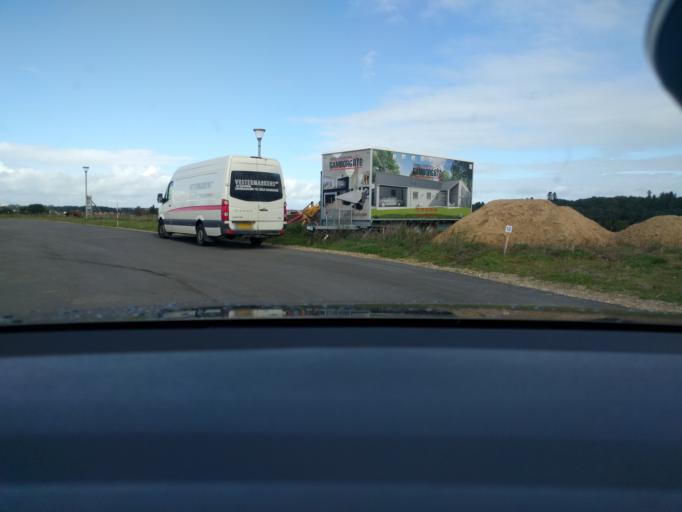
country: DK
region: Central Jutland
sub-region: Viborg Kommune
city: Viborg
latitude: 56.4316
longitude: 9.4237
